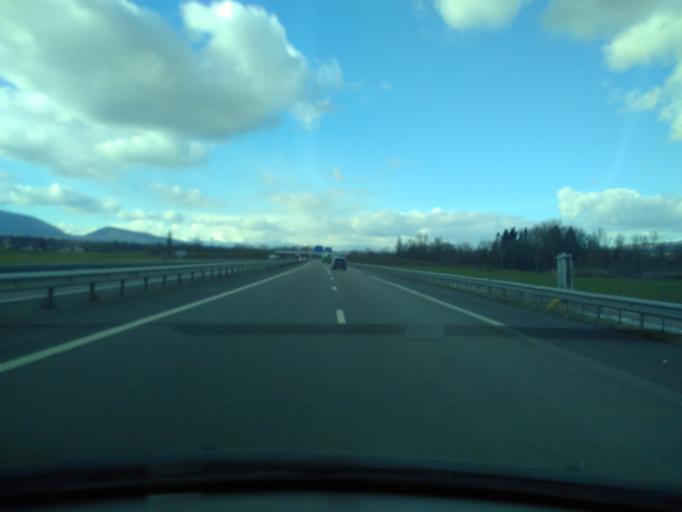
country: FR
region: Rhone-Alpes
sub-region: Departement de la Haute-Savoie
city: Arenthon
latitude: 46.1143
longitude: 6.3378
